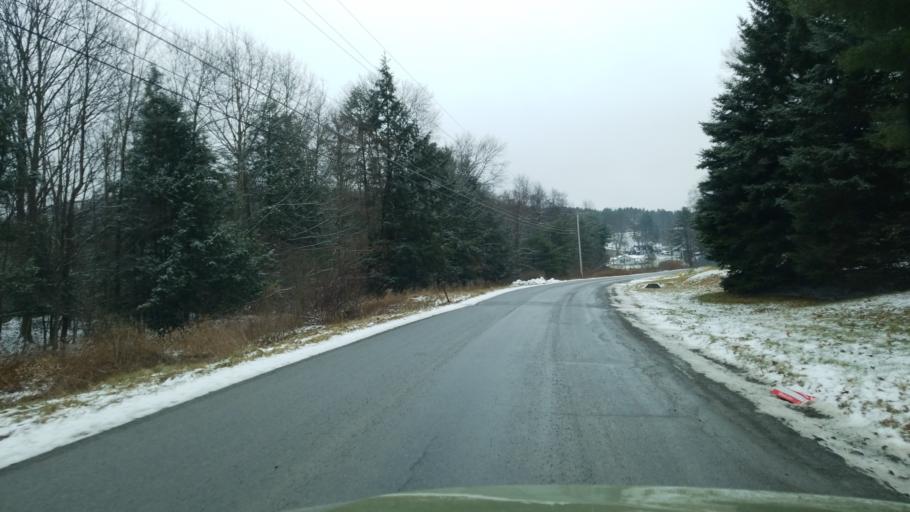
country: US
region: Pennsylvania
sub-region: Jefferson County
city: Sykesville
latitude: 41.0592
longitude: -78.8180
